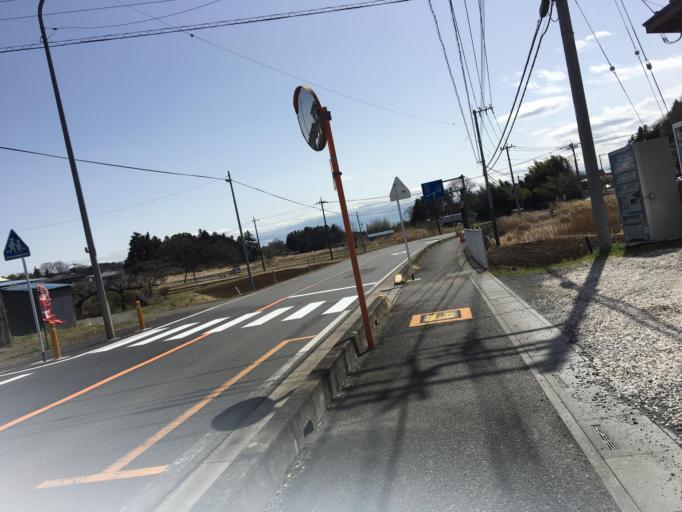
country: JP
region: Saitama
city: Morohongo
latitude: 35.9947
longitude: 139.3339
